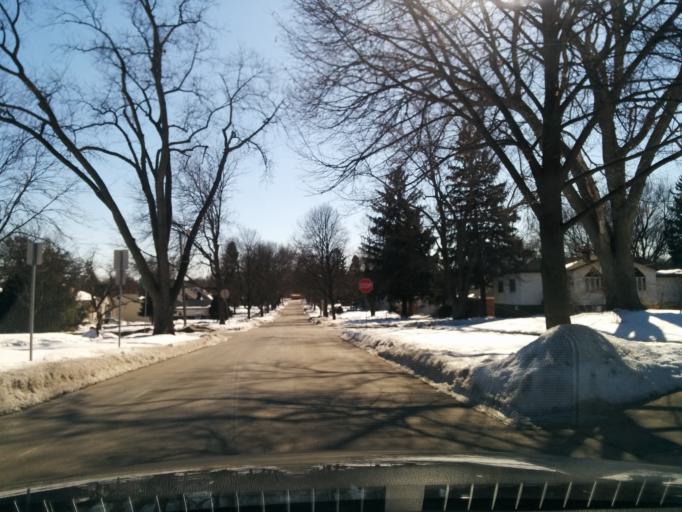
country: US
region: Illinois
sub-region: DuPage County
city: Villa Park
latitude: 41.8929
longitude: -87.9872
